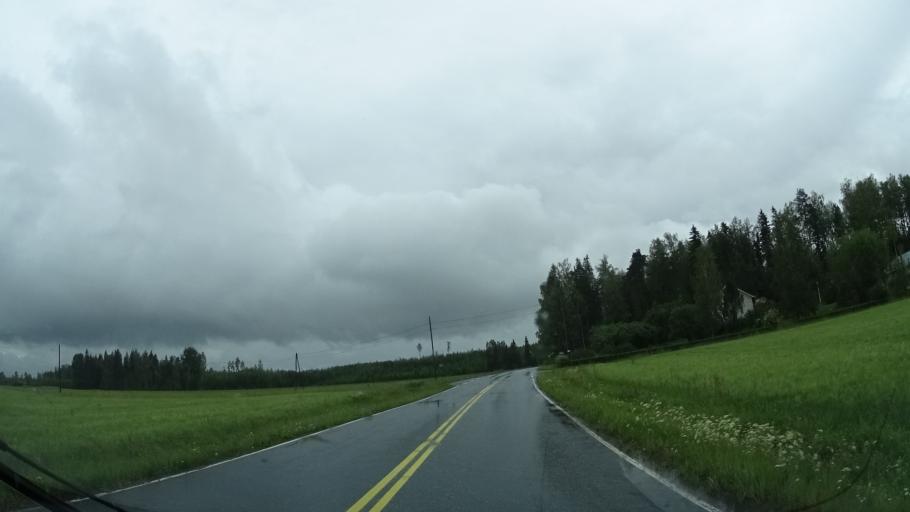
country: FI
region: Haeme
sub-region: Forssa
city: Humppila
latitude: 60.9957
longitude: 23.2536
